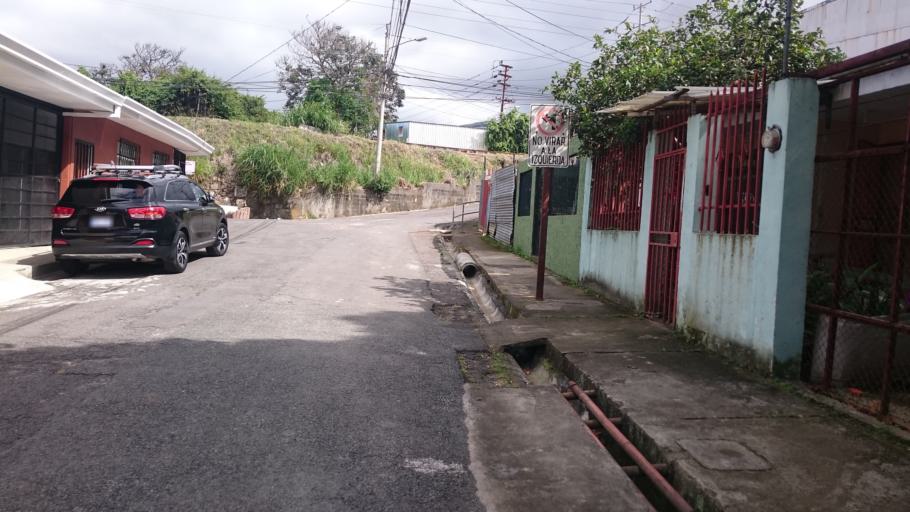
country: CR
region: San Jose
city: Calle Blancos
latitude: 9.9427
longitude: -84.0700
